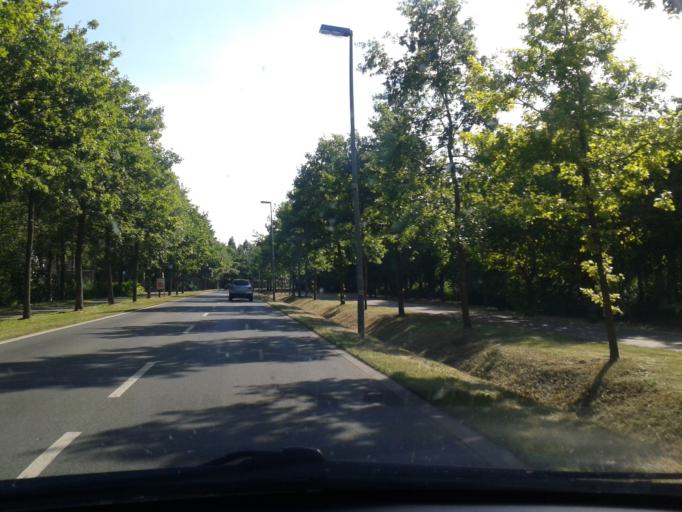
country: DE
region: North Rhine-Westphalia
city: Bad Lippspringe
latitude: 51.7816
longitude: 8.8073
